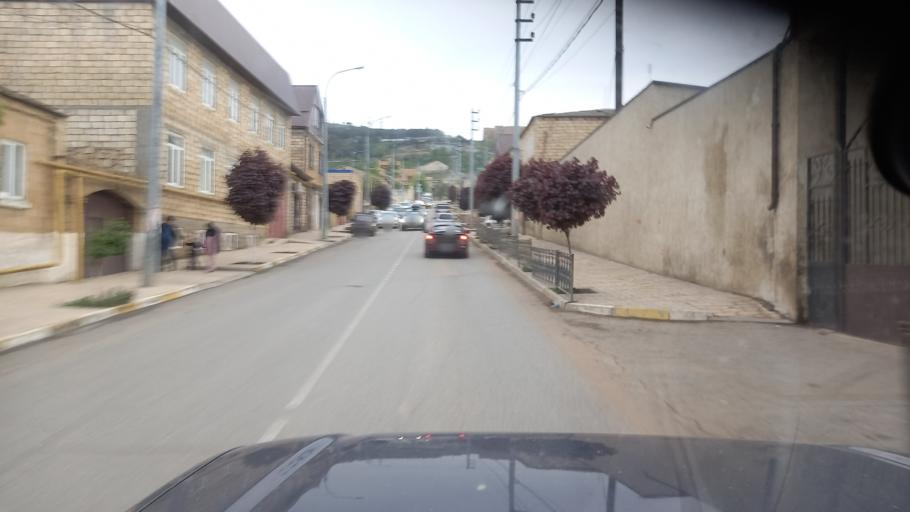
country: RU
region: Dagestan
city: Derbent
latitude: 42.0536
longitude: 48.2827
